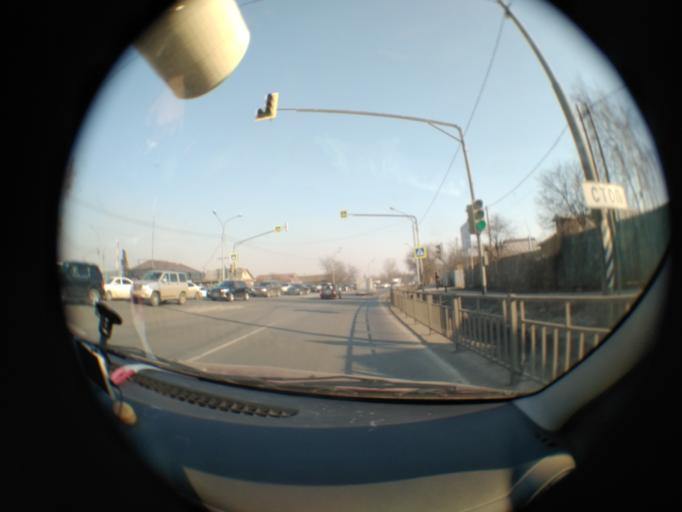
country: RU
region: Moskovskaya
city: Ostrovtsy
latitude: 55.5894
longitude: 38.0066
